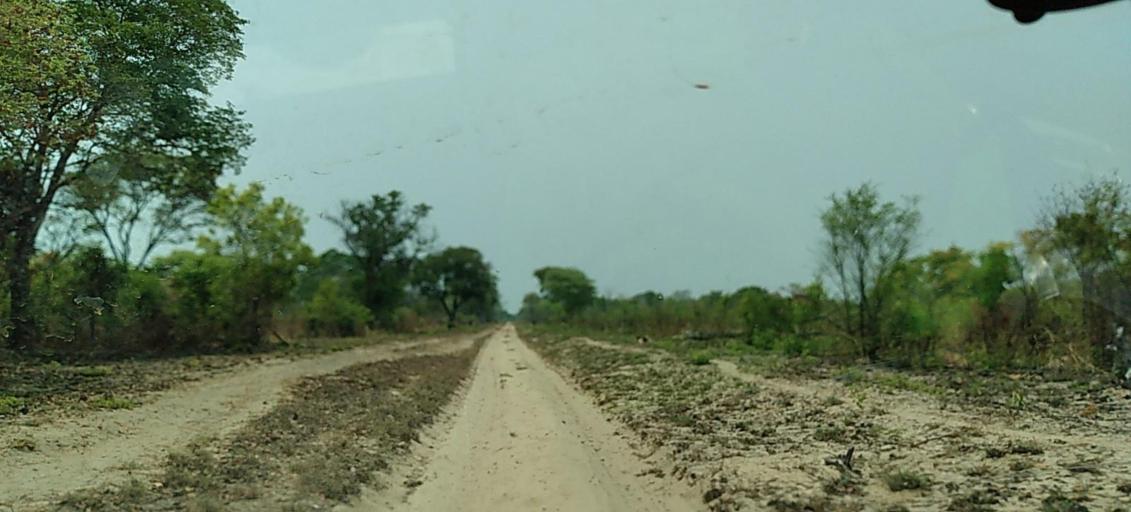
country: ZM
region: Western
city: Lukulu
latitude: -14.1490
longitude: 23.2940
